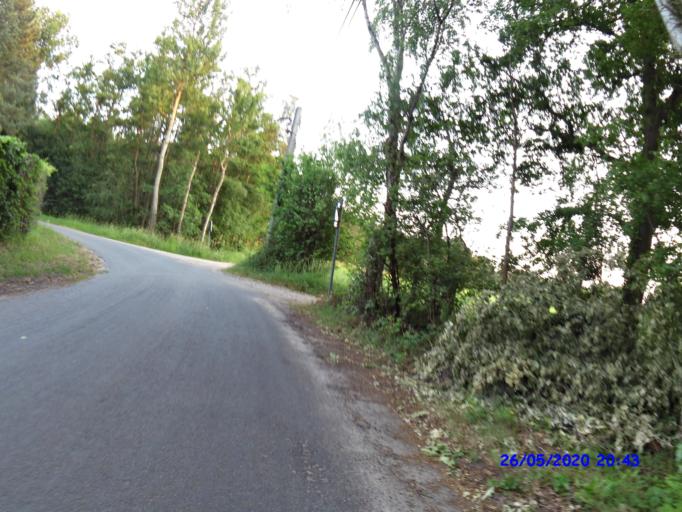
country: BE
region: Flanders
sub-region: Provincie Antwerpen
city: Geel
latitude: 51.1905
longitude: 5.0160
